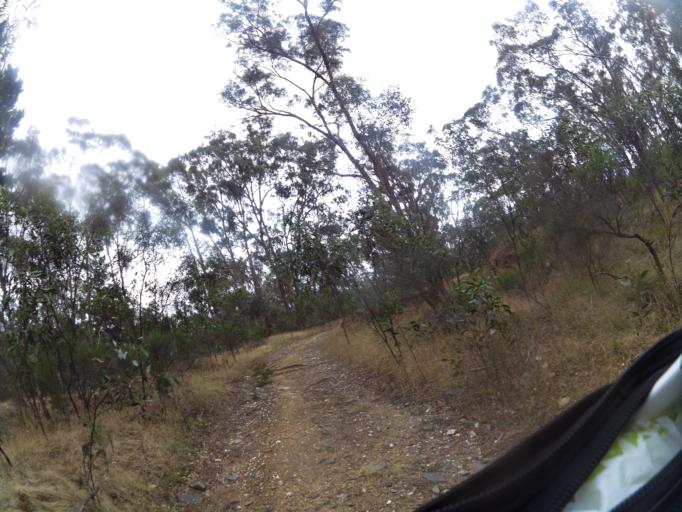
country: AU
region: Victoria
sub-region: Mount Alexander
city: Castlemaine
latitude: -37.0716
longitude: 144.2551
